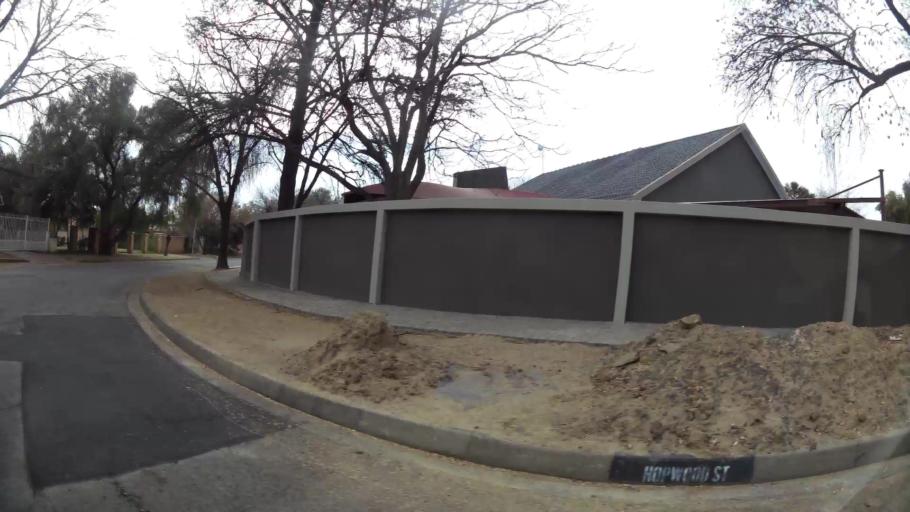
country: ZA
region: Orange Free State
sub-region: Mangaung Metropolitan Municipality
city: Bloemfontein
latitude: -29.1204
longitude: 26.1936
